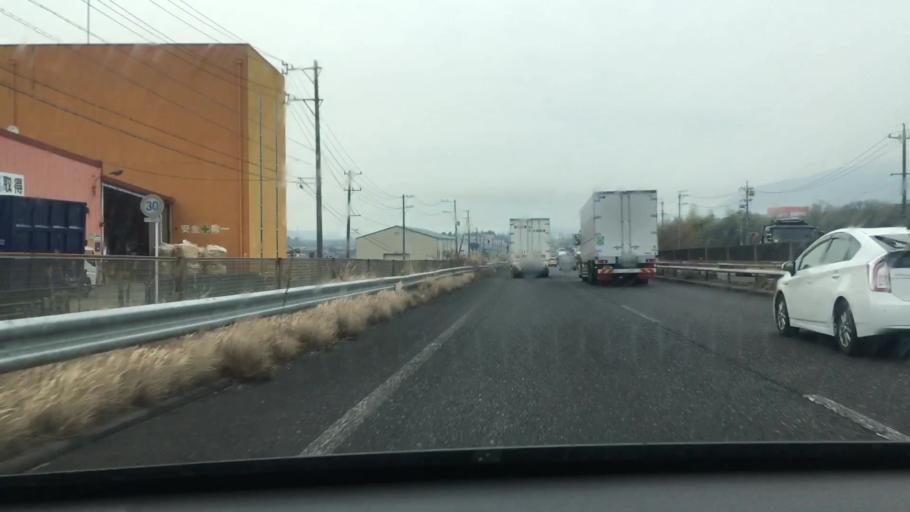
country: JP
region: Mie
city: Ueno-ebisumachi
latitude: 34.7997
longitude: 136.1819
